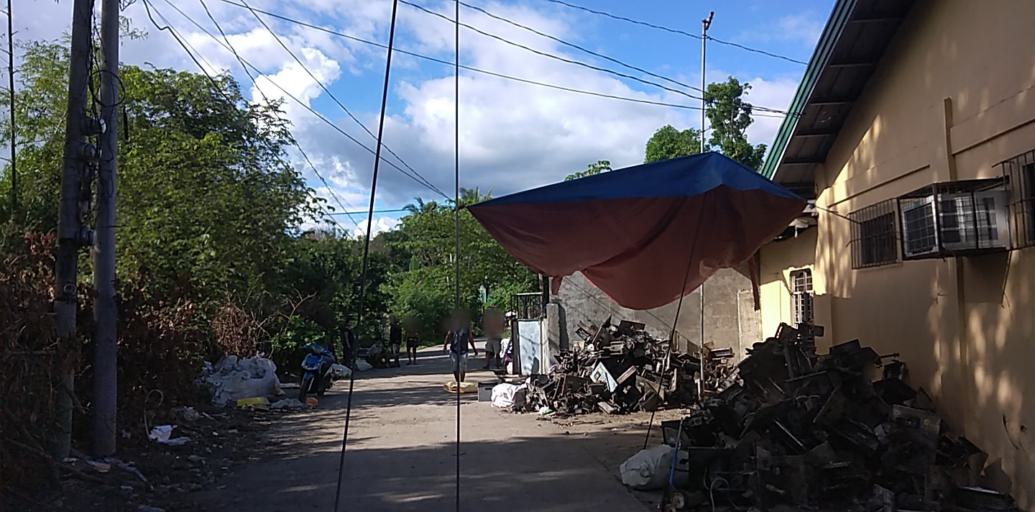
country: PH
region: Central Luzon
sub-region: Province of Pampanga
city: Arayat
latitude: 15.1415
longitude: 120.7714
